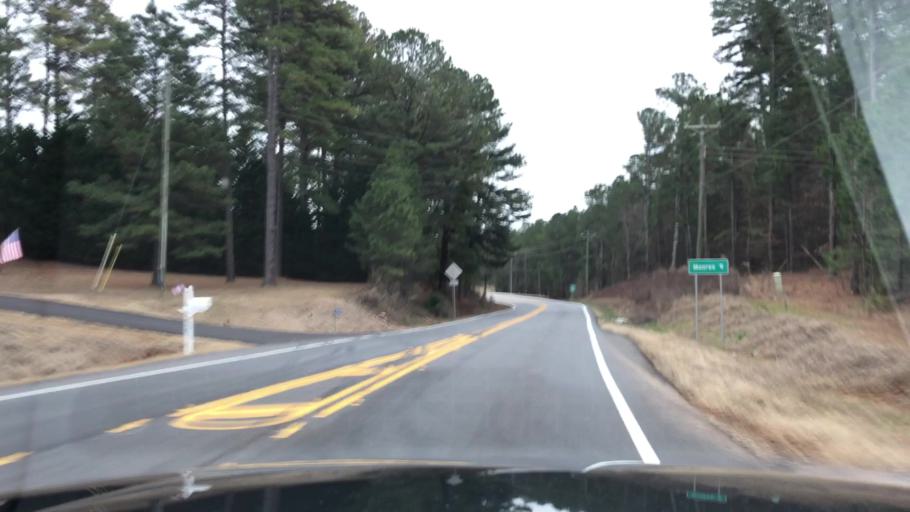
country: US
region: Georgia
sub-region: Barrow County
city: Auburn
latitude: 33.9003
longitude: -83.7996
